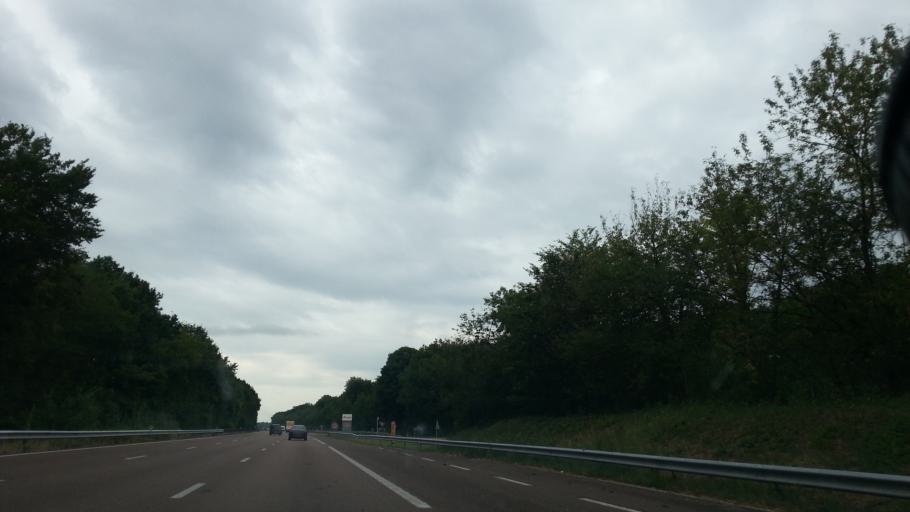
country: FR
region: Bourgogne
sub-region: Departement de Saone-et-Loire
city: Champforgeuil
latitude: 46.8620
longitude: 4.8217
